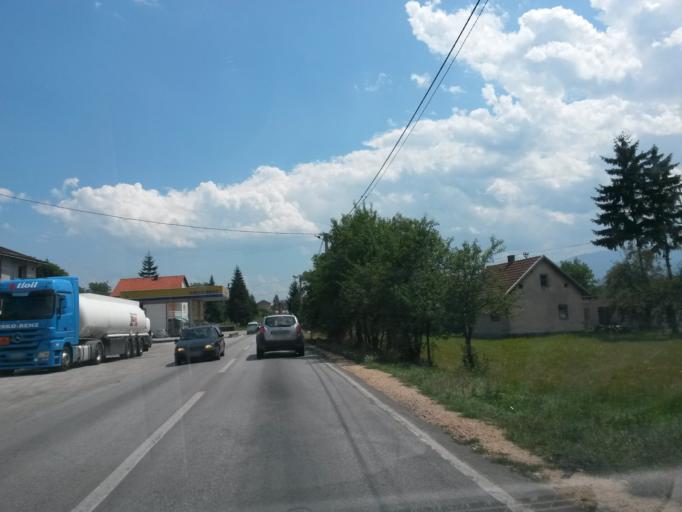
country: BA
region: Federation of Bosnia and Herzegovina
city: Vitez
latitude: 44.1860
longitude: 17.7445
